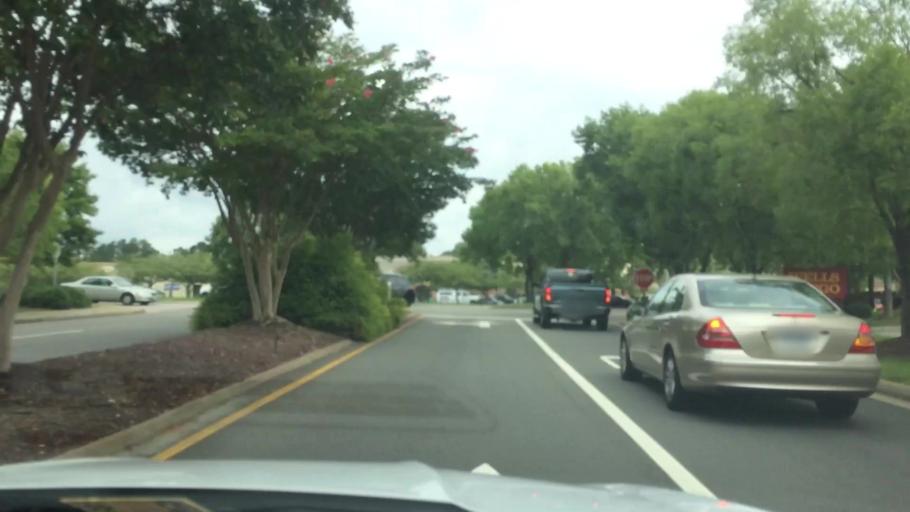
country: US
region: Virginia
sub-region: James City County
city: Williamsburg
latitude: 37.2709
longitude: -76.7578
